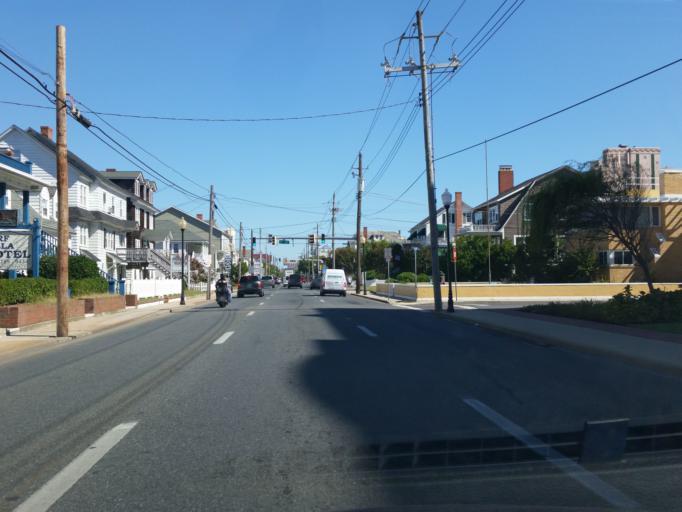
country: US
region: Maryland
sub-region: Worcester County
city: Ocean City
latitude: 38.3383
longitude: -75.0826
